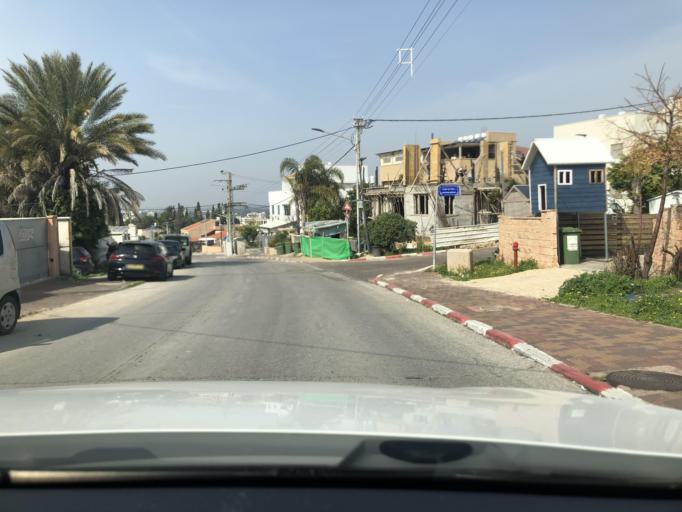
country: IL
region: Central District
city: Rosh Ha'Ayin
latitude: 32.0926
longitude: 34.9591
